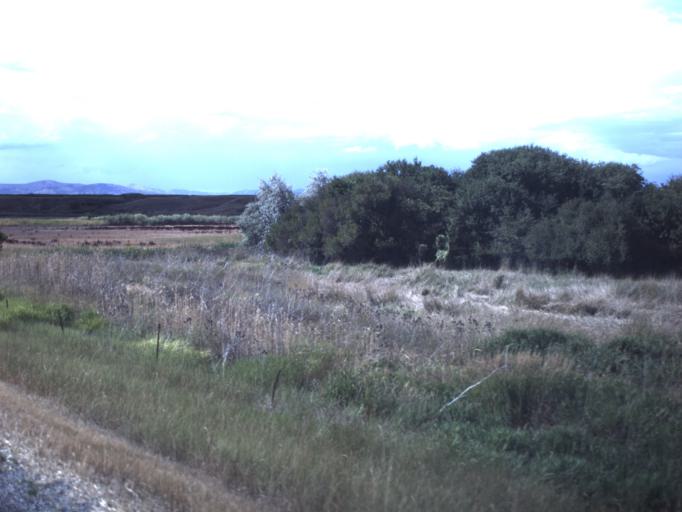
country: US
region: Utah
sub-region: Cache County
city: Richmond
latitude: 41.9240
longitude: -111.8449
